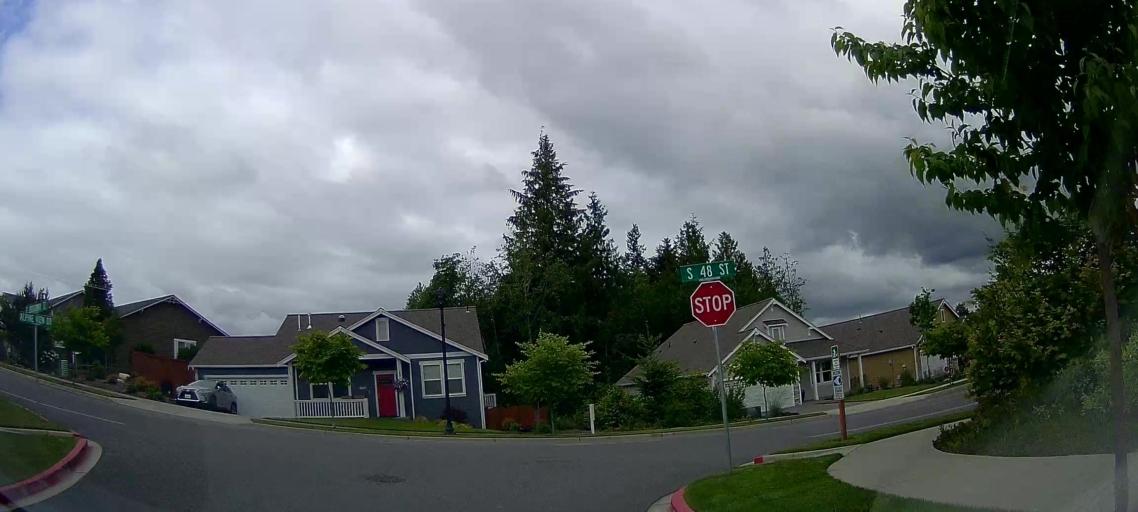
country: US
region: Washington
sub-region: Skagit County
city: Big Lake
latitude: 48.4168
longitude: -122.2804
